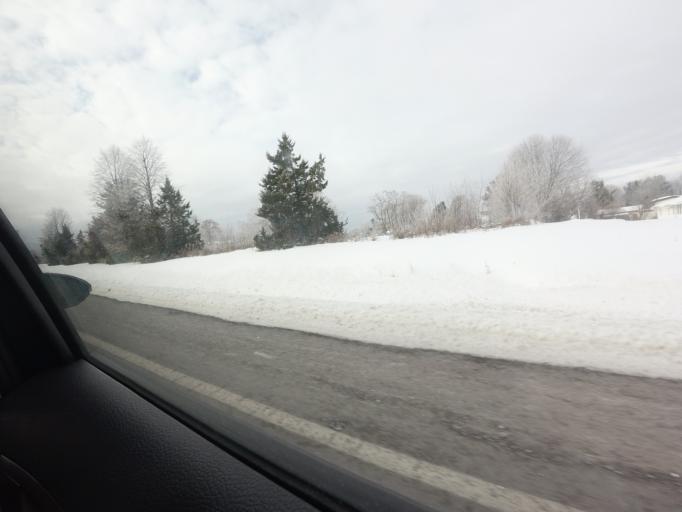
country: CA
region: New Brunswick
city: Oromocto
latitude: 45.8492
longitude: -66.4679
